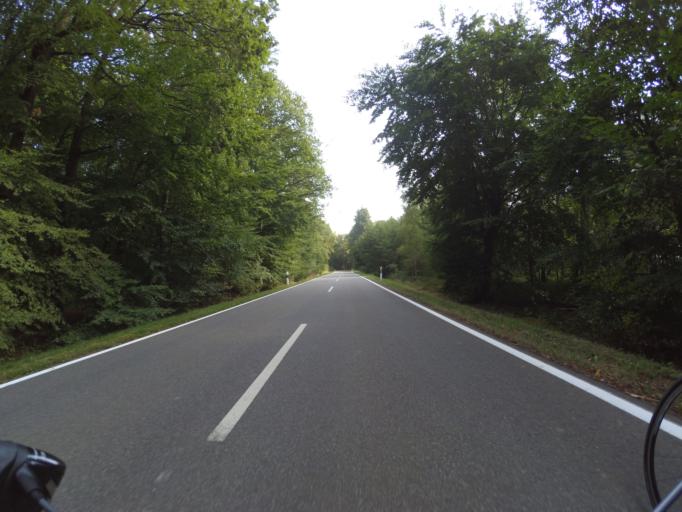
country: DE
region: Rheinland-Pfalz
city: Burgen
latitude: 49.8551
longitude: 6.9779
